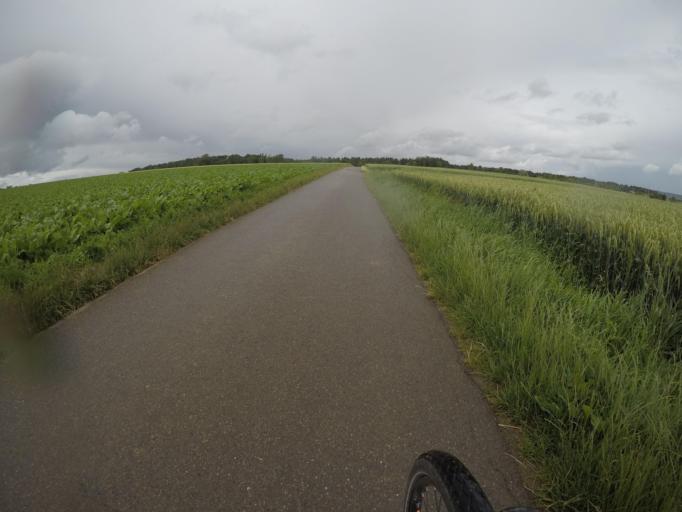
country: DE
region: Baden-Wuerttemberg
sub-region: Regierungsbezirk Stuttgart
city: Bondorf
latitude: 48.5621
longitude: 8.8290
